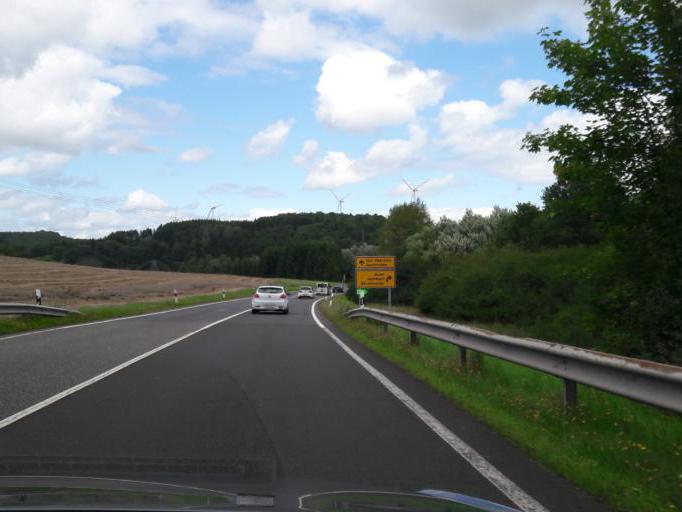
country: DE
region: Rheinland-Pfalz
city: Fohren-Linden
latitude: 49.5832
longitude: 7.2922
